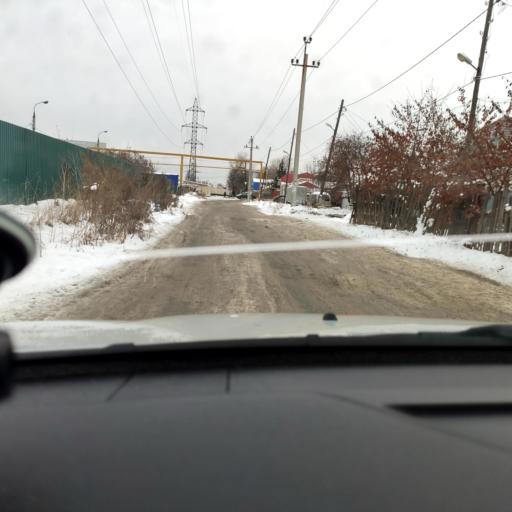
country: RU
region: Samara
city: Samara
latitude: 53.1827
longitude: 50.2375
